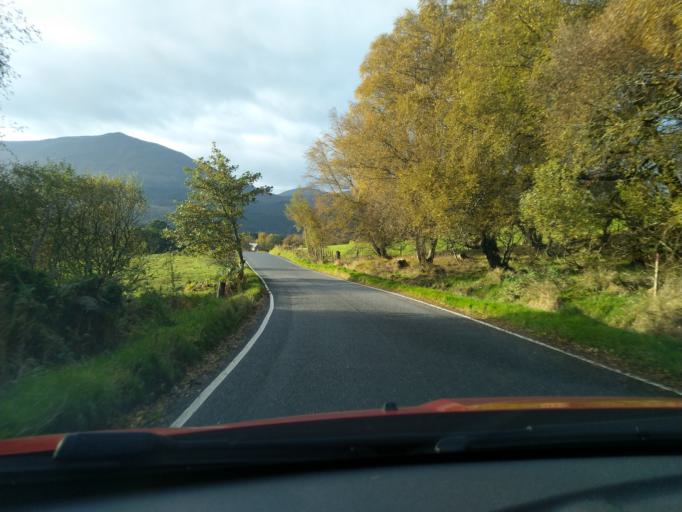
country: GB
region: Scotland
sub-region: Perth and Kinross
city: Aberfeldy
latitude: 56.7129
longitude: -4.1231
